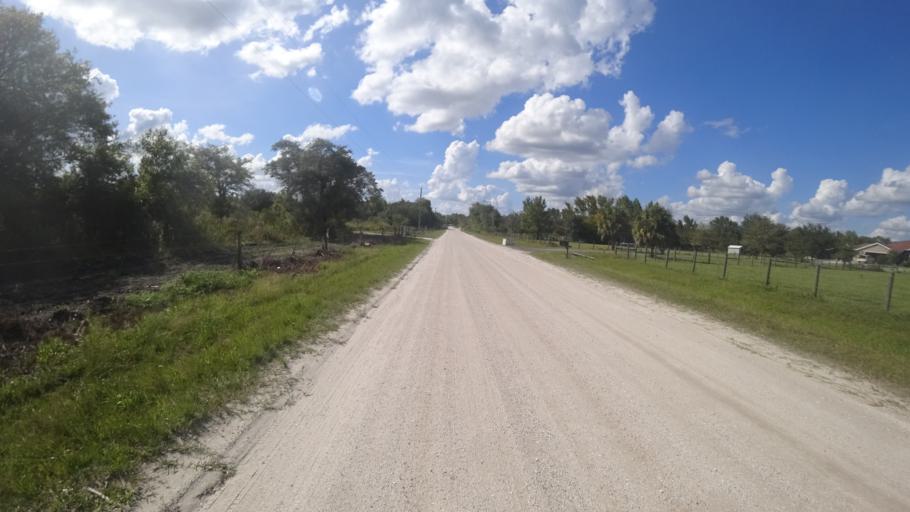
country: US
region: Florida
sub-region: Sarasota County
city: Lake Sarasota
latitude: 27.4223
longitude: -82.1368
